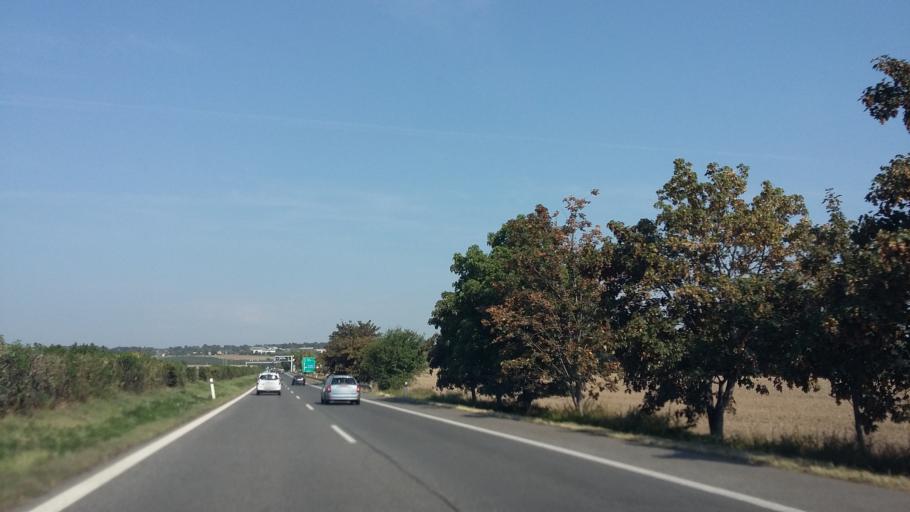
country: CZ
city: Ohrazenice
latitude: 50.6081
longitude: 15.1172
